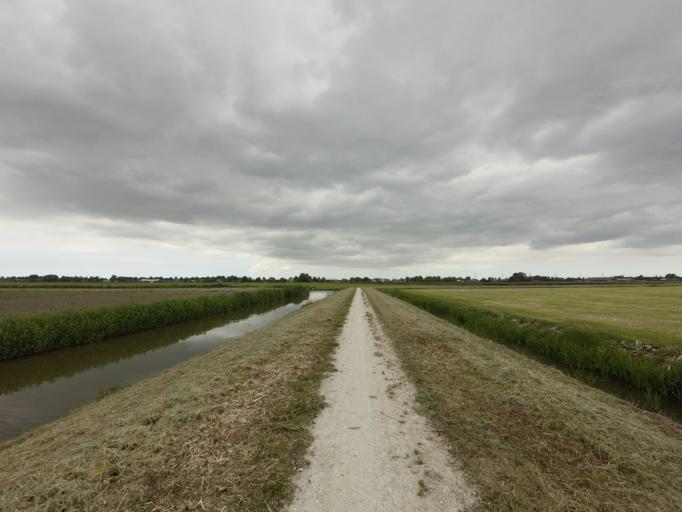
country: NL
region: North Holland
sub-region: Gemeente Hoorn
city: Hoorn
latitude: 52.6102
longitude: 4.9730
